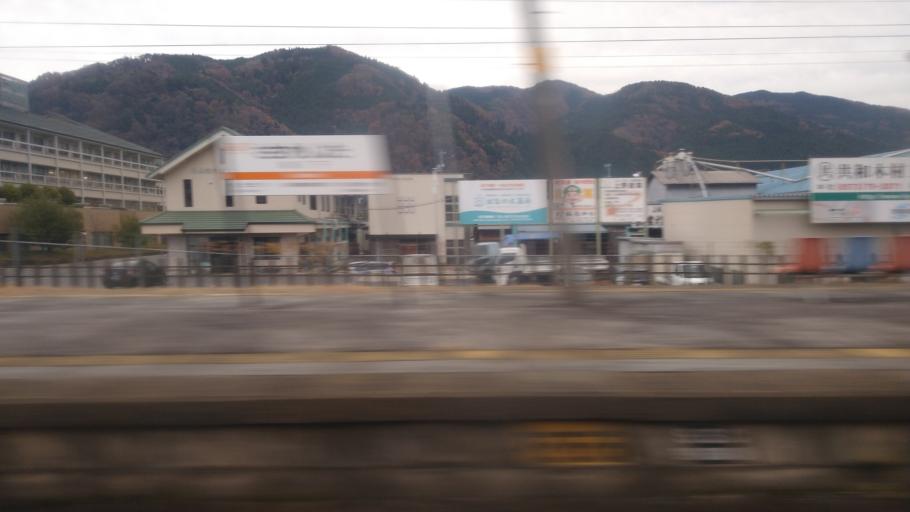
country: JP
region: Gifu
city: Nakatsugawa
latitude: 35.5745
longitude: 137.5311
